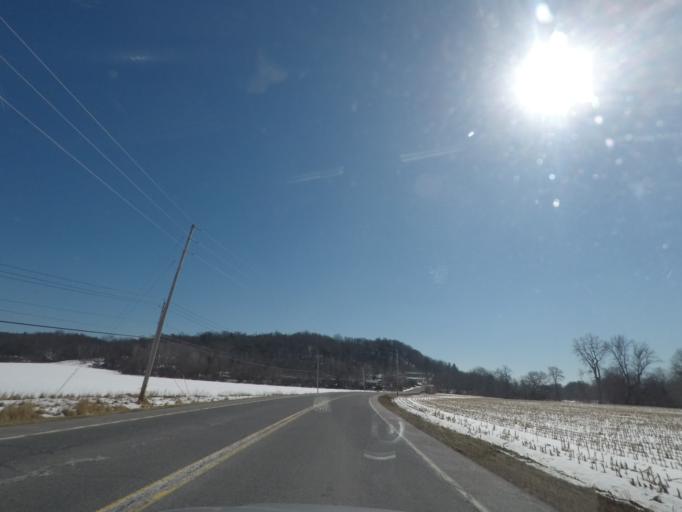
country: US
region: New York
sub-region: Saratoga County
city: Stillwater
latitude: 42.9342
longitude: -73.6459
